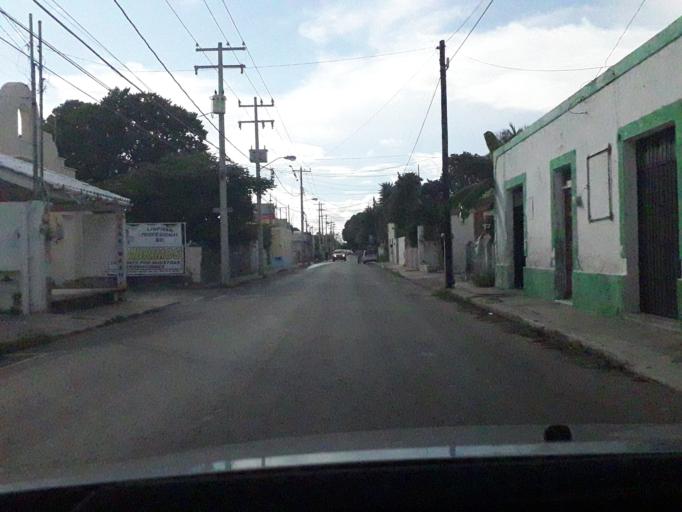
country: MX
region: Yucatan
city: Merida
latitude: 21.0119
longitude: -89.6350
